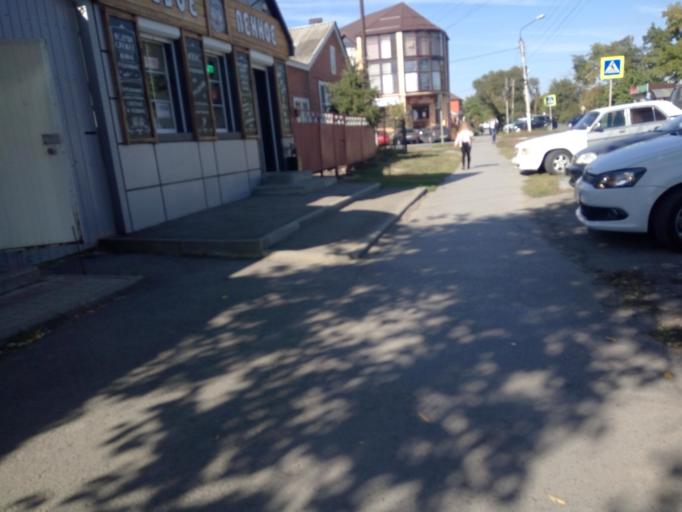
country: RU
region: Rostov
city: Bataysk
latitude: 47.1413
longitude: 39.7360
